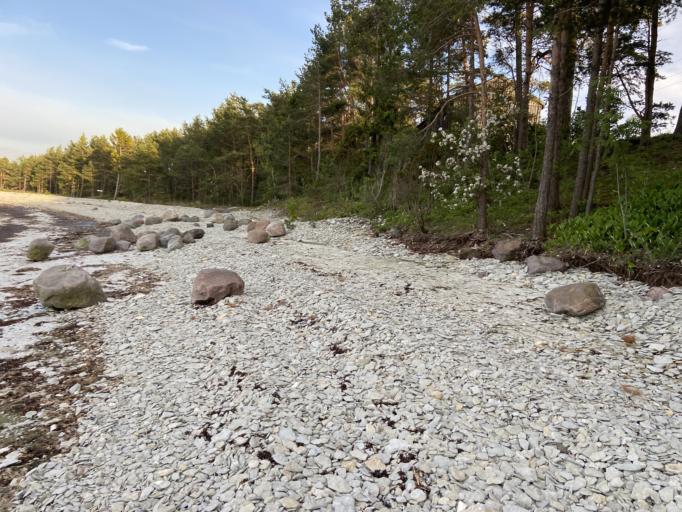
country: EE
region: Harju
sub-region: Paldiski linn
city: Paldiski
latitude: 59.2714
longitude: 23.7347
